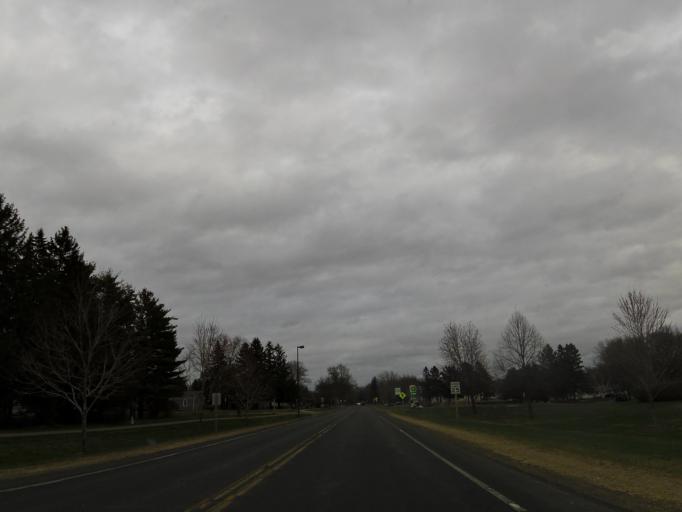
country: US
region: Wisconsin
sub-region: Saint Croix County
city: New Richmond
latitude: 45.1188
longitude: -92.5510
